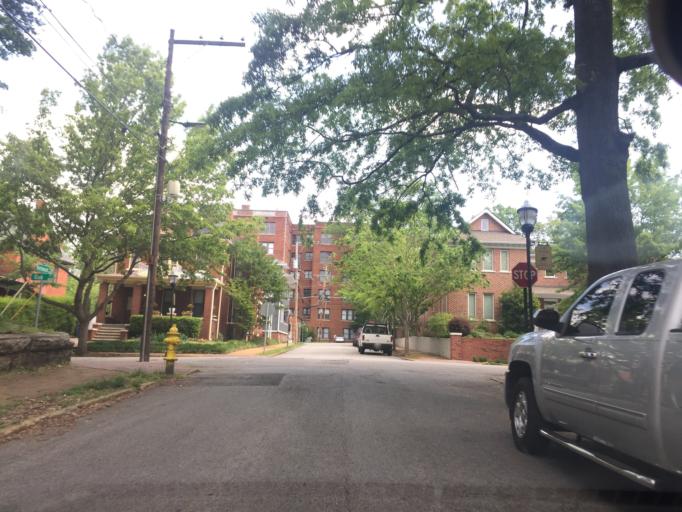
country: US
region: Tennessee
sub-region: Hamilton County
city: Chattanooga
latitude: 35.0433
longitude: -85.2923
